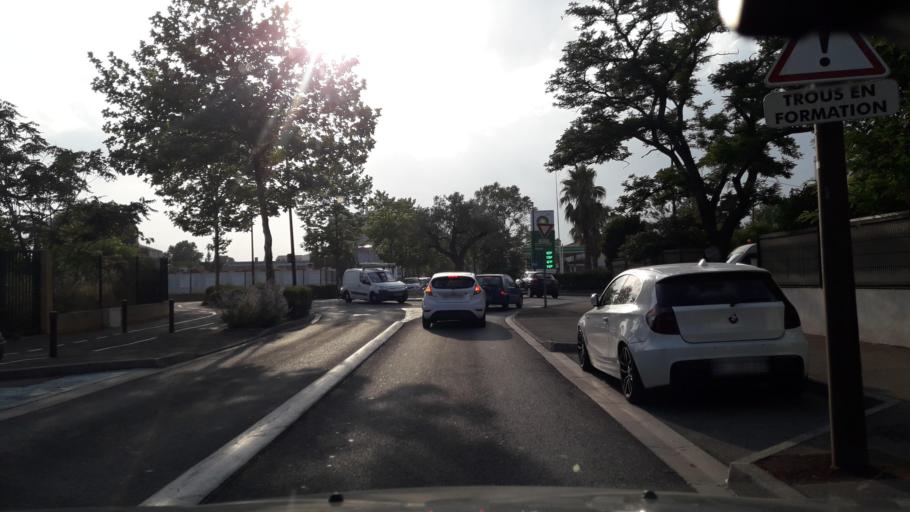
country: FR
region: Provence-Alpes-Cote d'Azur
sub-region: Departement du Var
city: Saint-Raphael
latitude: 43.4299
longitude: 6.7588
